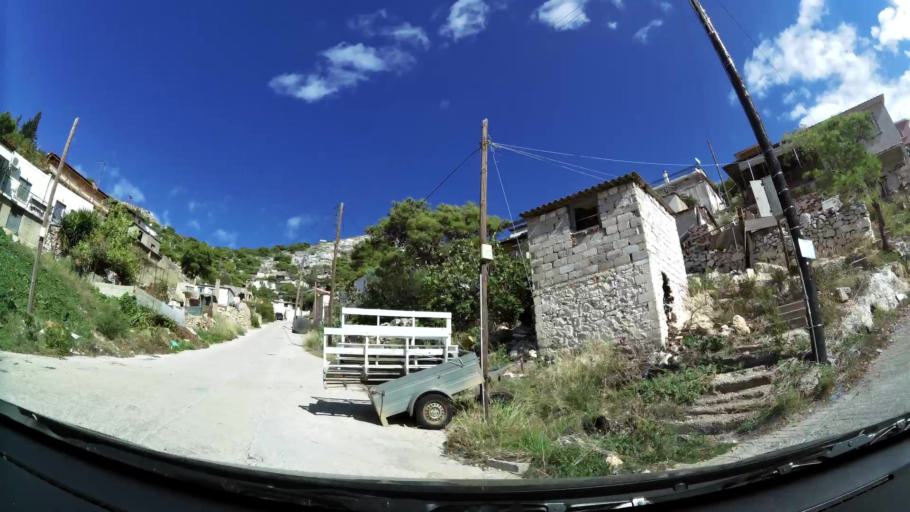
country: GR
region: Attica
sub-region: Nomos Piraios
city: Perama
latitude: 37.9688
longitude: 23.5737
